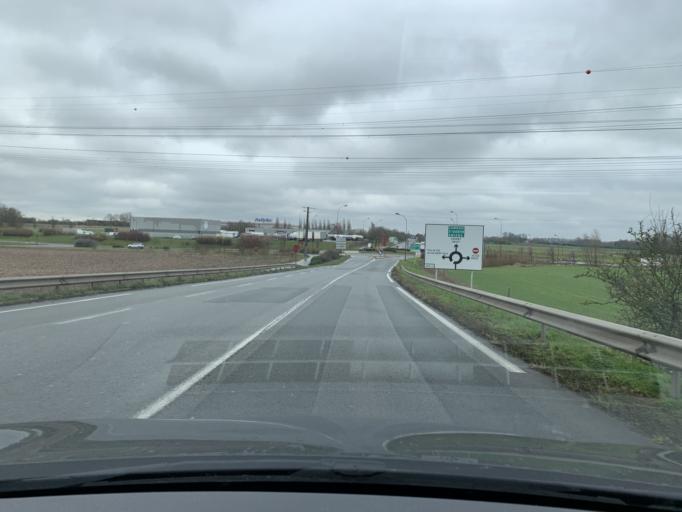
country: FR
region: Nord-Pas-de-Calais
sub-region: Departement du Nord
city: Hordain
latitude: 50.2513
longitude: 3.3223
